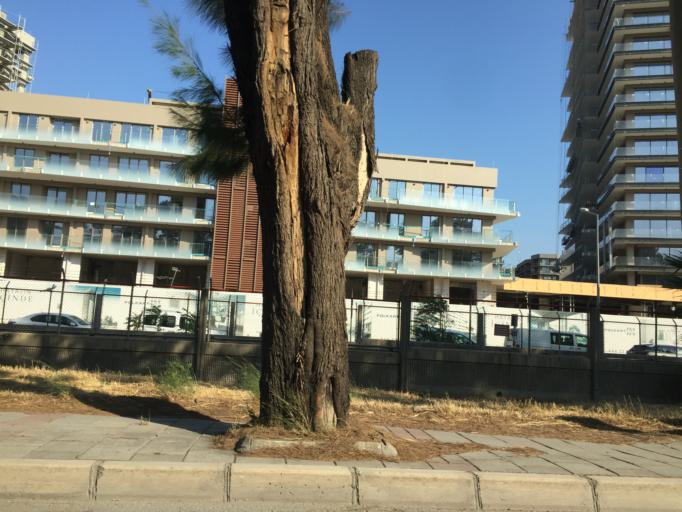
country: TR
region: Izmir
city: Buca
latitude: 38.4464
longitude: 27.1876
